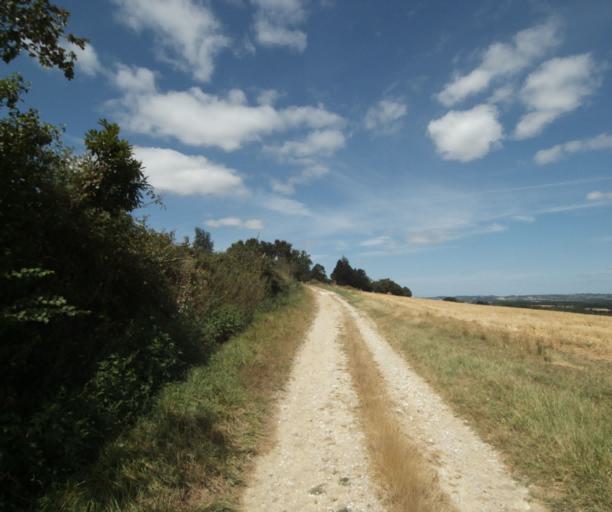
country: FR
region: Midi-Pyrenees
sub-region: Departement du Tarn
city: Soreze
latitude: 43.4909
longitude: 2.0703
